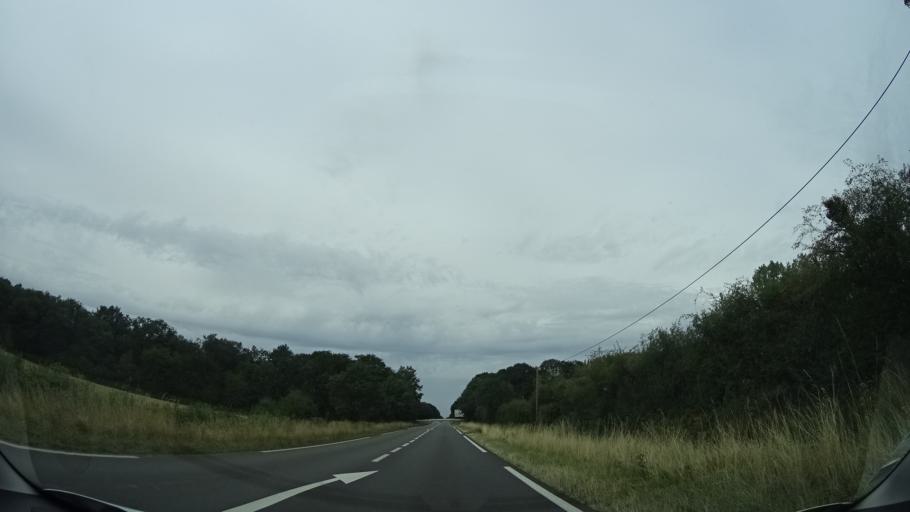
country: FR
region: Pays de la Loire
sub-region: Departement de la Mayenne
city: Meslay-du-Maine
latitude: 47.9814
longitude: -0.6109
